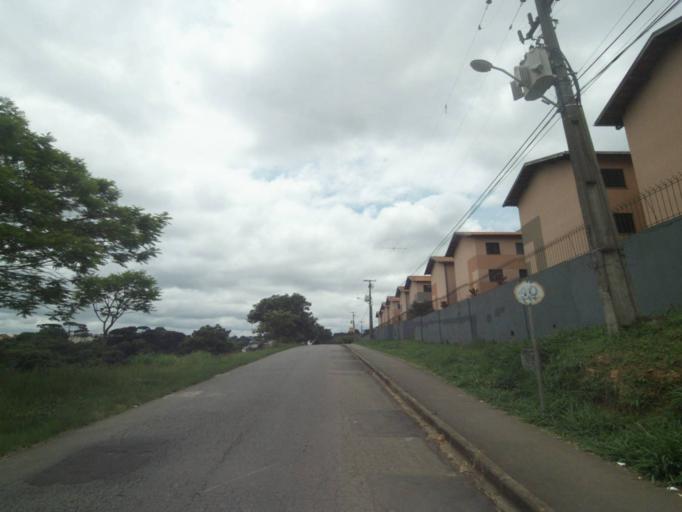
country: BR
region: Parana
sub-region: Curitiba
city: Curitiba
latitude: -25.3882
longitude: -49.2930
